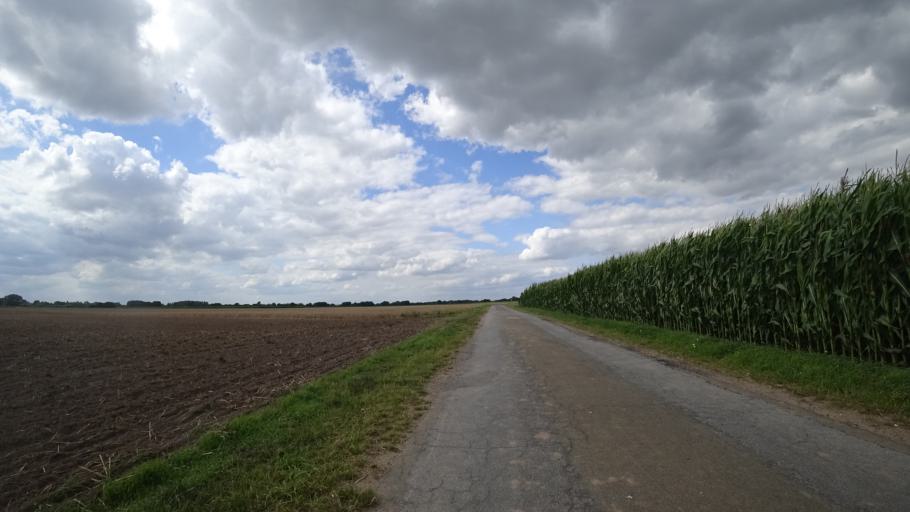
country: DE
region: Lower Saxony
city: Raddestorf
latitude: 52.4350
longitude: 9.0242
